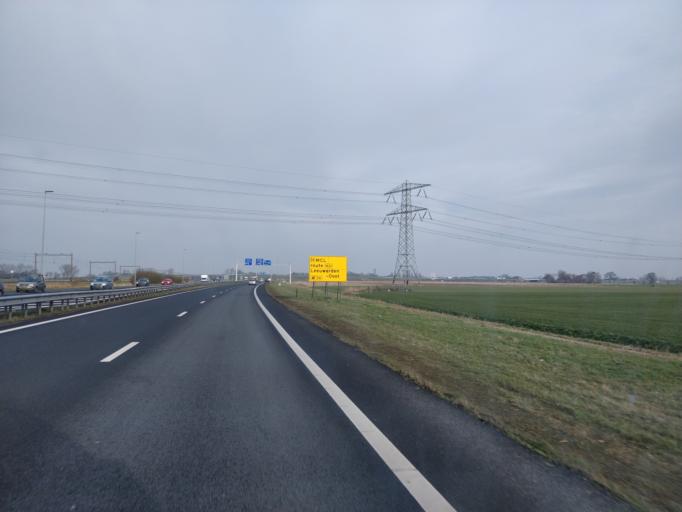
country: NL
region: Friesland
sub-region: Gemeente Leeuwarden
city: Wirdum
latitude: 53.1496
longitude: 5.7937
